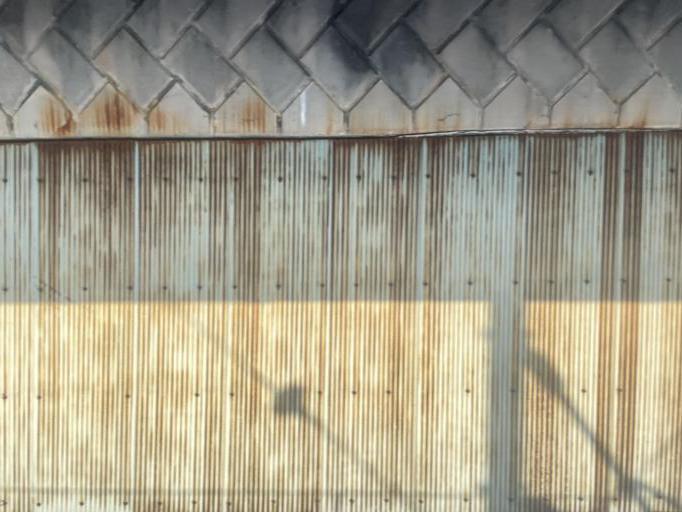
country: JP
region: Gunma
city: Nakanojomachi
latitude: 36.5774
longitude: 138.8742
